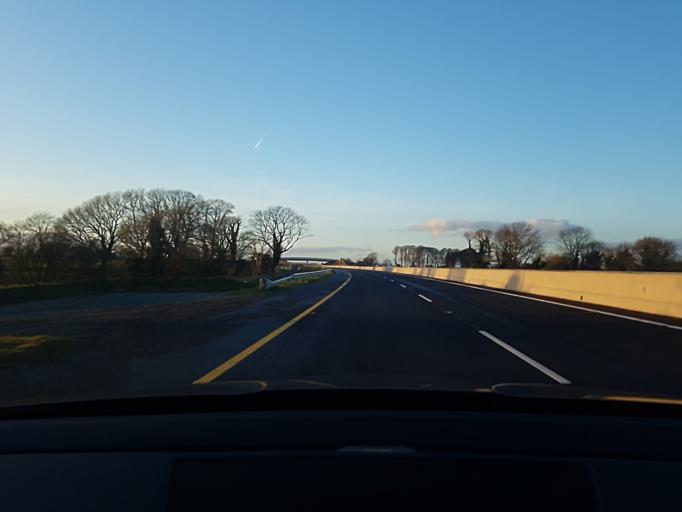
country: IE
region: Connaught
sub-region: County Galway
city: Tuam
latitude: 53.4616
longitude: -8.8513
